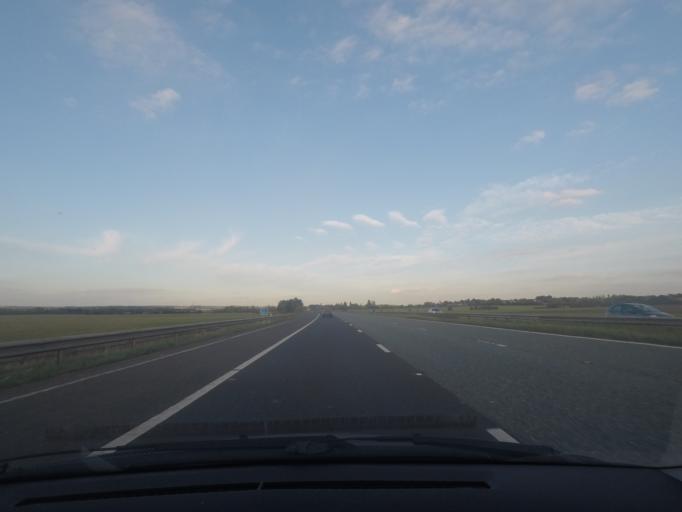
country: GB
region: England
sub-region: North Lincolnshire
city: Brigg
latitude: 53.5650
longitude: -0.4829
